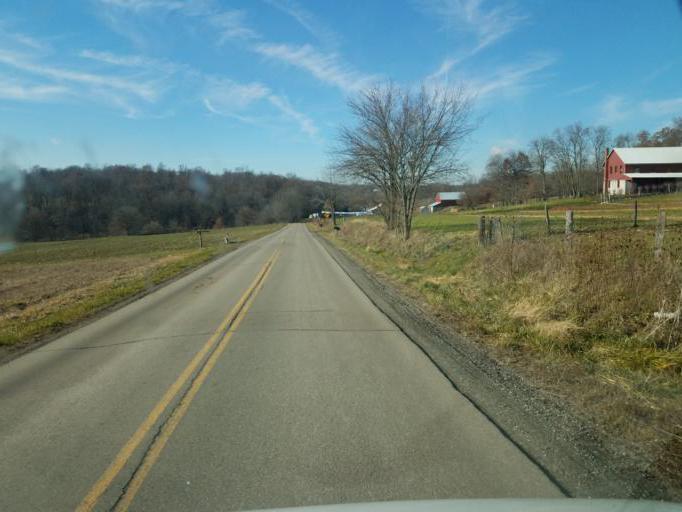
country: US
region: Ohio
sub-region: Wayne County
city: Dalton
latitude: 40.7338
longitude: -81.7189
